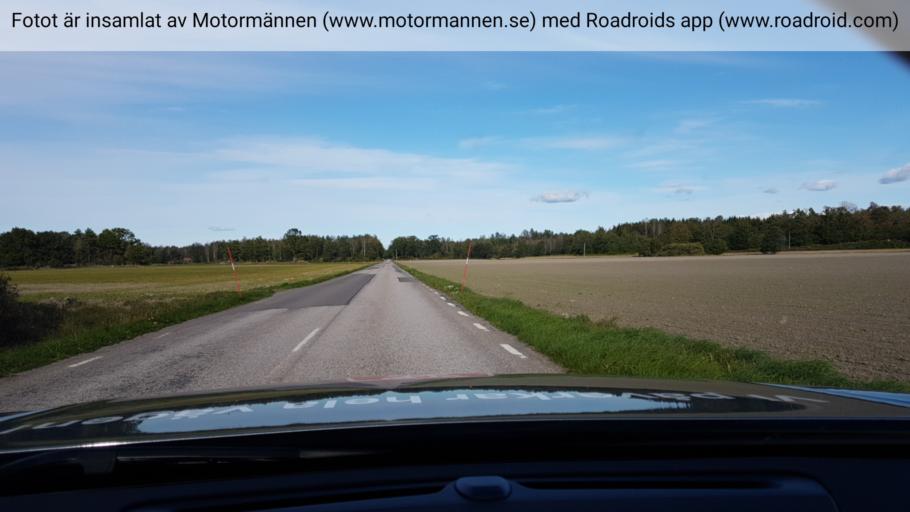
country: SE
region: Kalmar
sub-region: Vasterviks Kommun
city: Forserum
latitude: 58.0353
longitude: 16.5944
